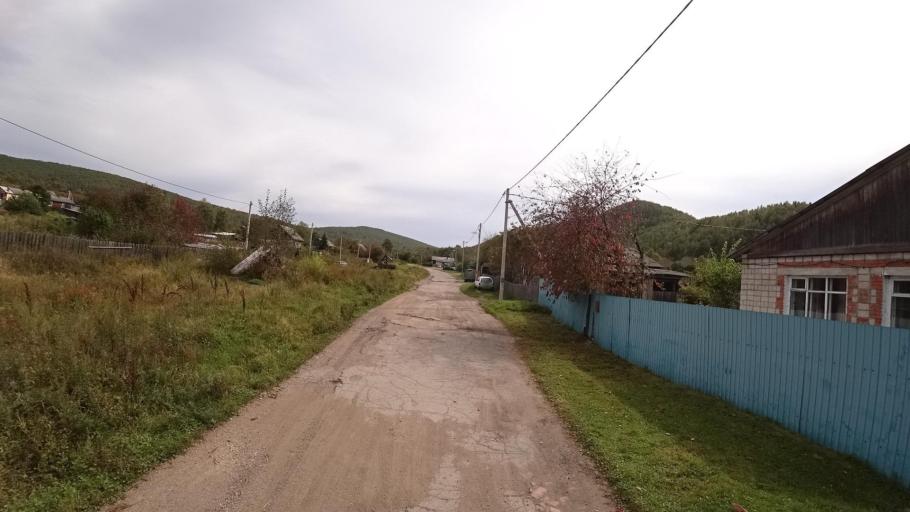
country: RU
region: Jewish Autonomous Oblast
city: Khingansk
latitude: 49.1231
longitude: 131.2045
